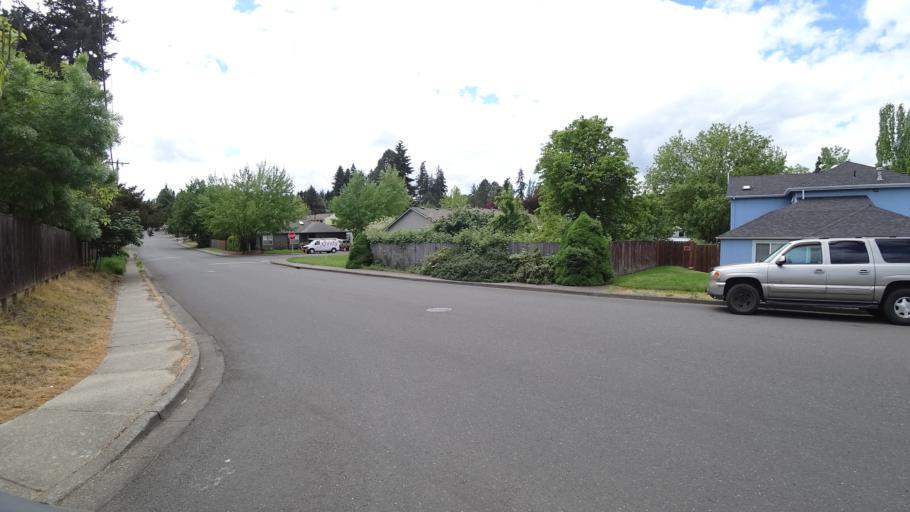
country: US
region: Oregon
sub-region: Washington County
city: Aloha
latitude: 45.4728
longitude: -122.8607
